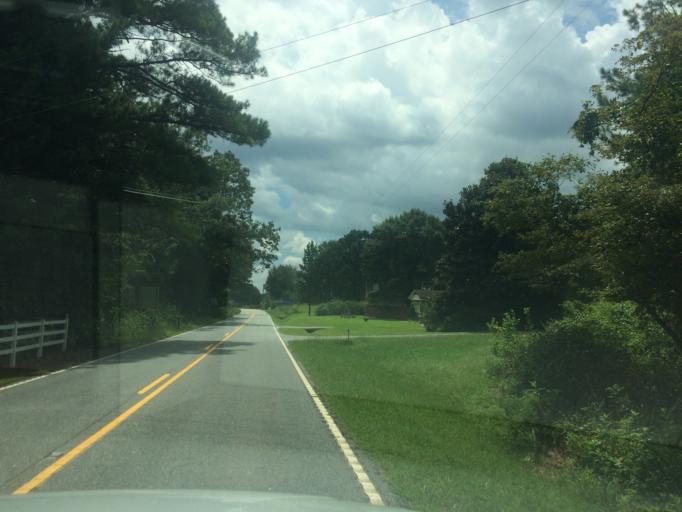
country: US
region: South Carolina
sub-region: Spartanburg County
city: Landrum
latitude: 35.1909
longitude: -82.0490
